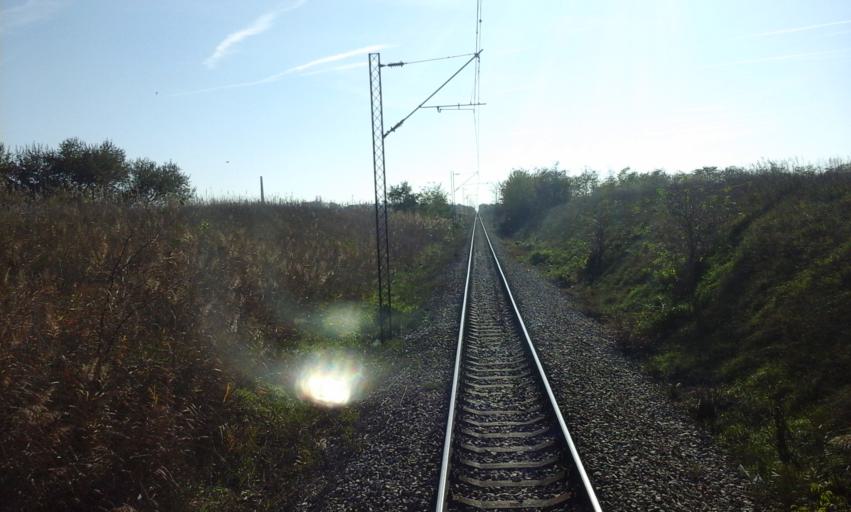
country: RS
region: Autonomna Pokrajina Vojvodina
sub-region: Severnobacki Okrug
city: Subotica
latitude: 46.0779
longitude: 19.6896
